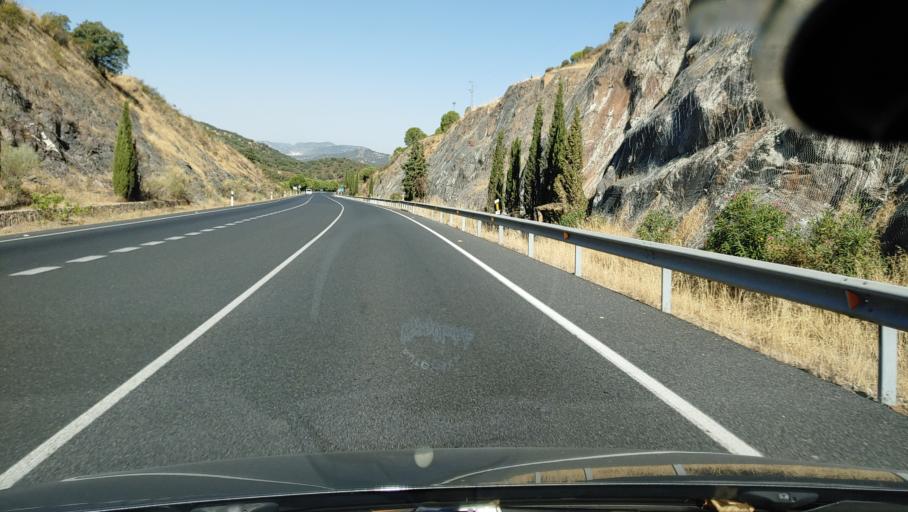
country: ES
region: Andalusia
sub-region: Province of Cordoba
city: Villaharta
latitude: 38.1117
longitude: -4.8823
